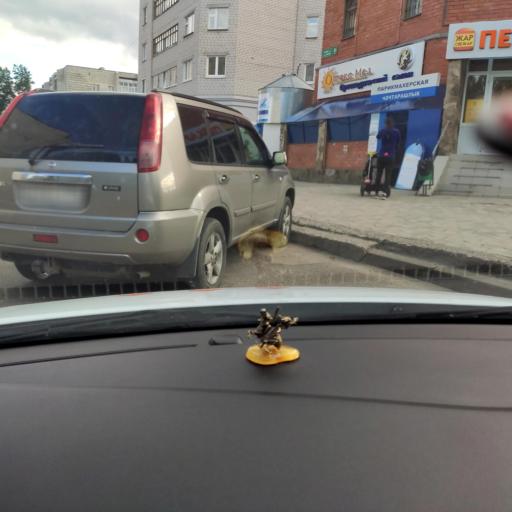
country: RU
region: Tatarstan
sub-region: Zelenodol'skiy Rayon
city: Zelenodolsk
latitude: 55.8511
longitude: 48.4940
